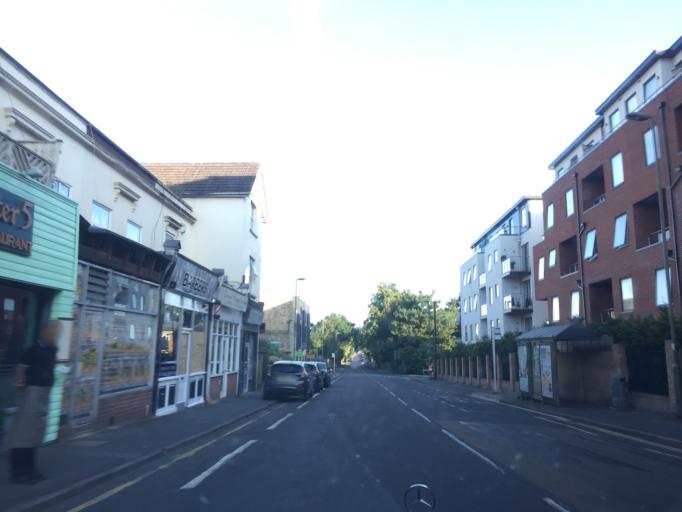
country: GB
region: England
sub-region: Surrey
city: Camberley
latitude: 51.3356
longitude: -0.7605
